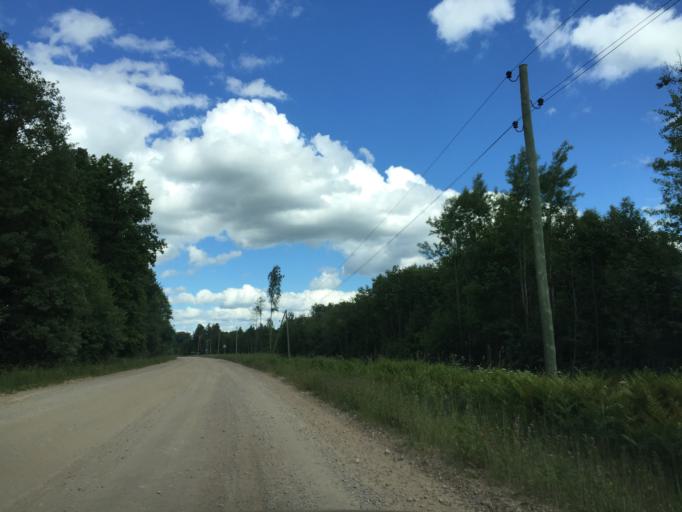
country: LV
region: Vecumnieki
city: Vecumnieki
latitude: 56.5049
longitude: 24.3924
